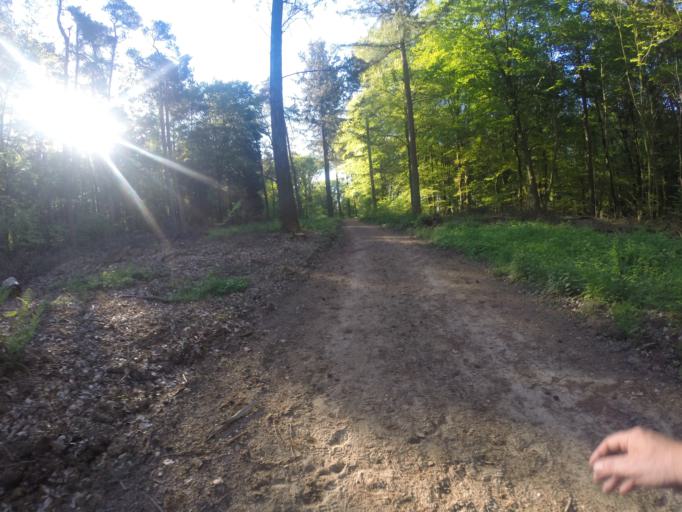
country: NL
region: Gelderland
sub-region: Gemeente Montferland
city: s-Heerenberg
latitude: 51.8936
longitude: 6.2280
